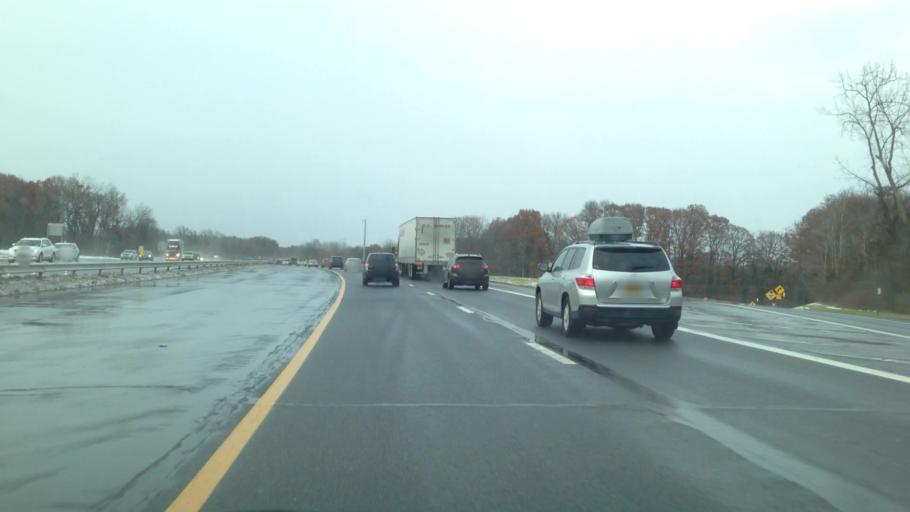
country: US
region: New York
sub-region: Rensselaer County
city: Castleton-on-Hudson
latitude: 42.5321
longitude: -73.7845
